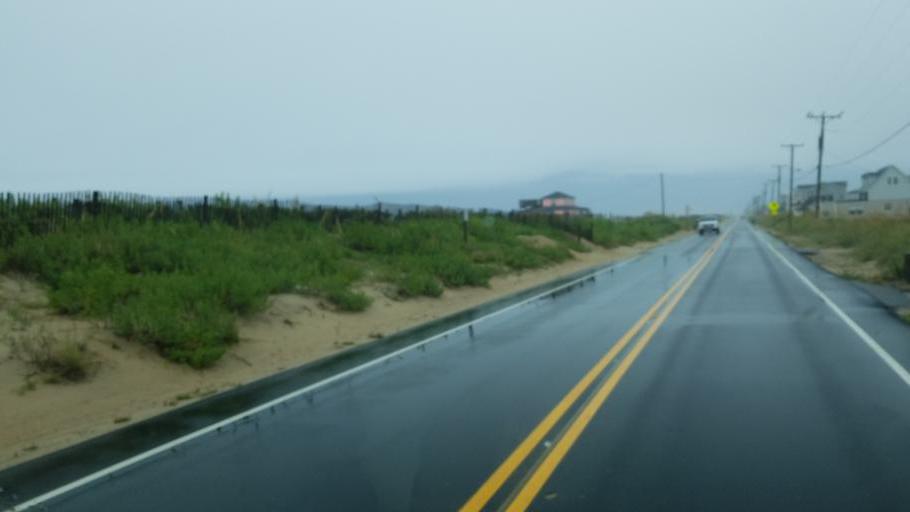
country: US
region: North Carolina
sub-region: Dare County
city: Kitty Hawk
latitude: 36.0708
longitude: -75.6931
